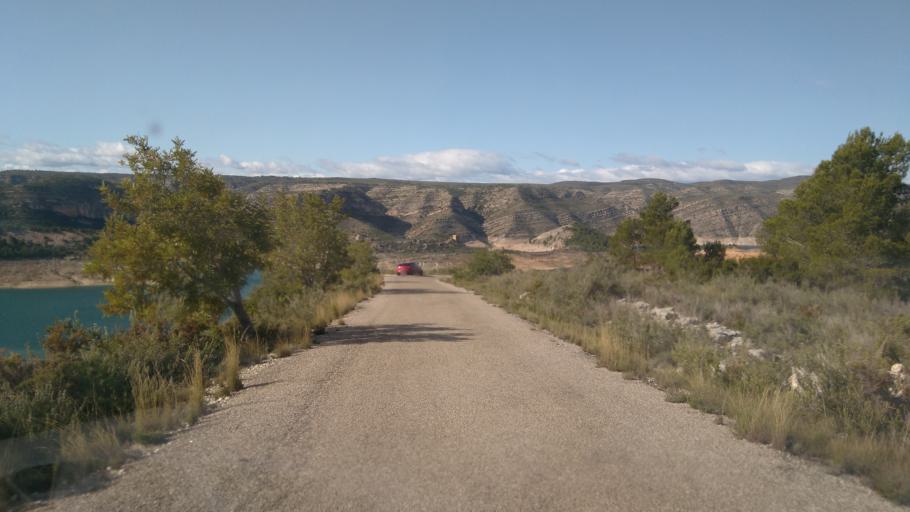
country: ES
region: Valencia
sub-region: Provincia de Valencia
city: Sumacarcer
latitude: 39.1510
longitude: -0.6511
